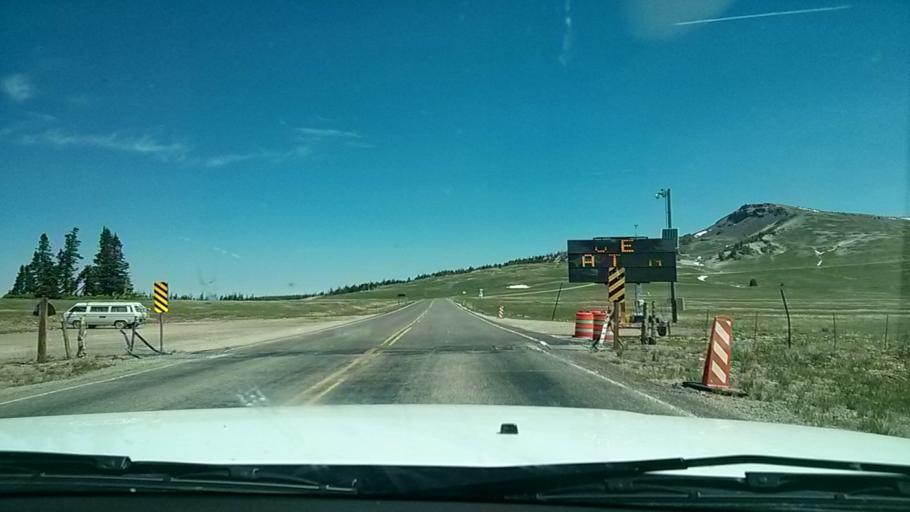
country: US
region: Utah
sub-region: Iron County
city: Parowan
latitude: 37.6617
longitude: -112.8377
